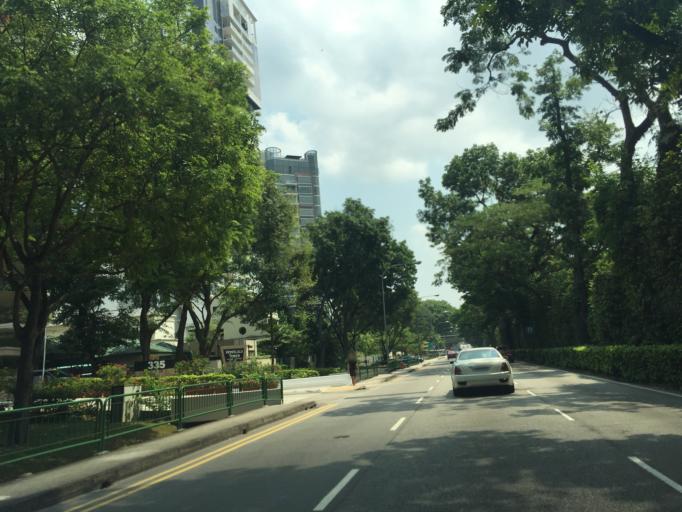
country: SG
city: Singapore
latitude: 1.3184
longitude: 103.8317
